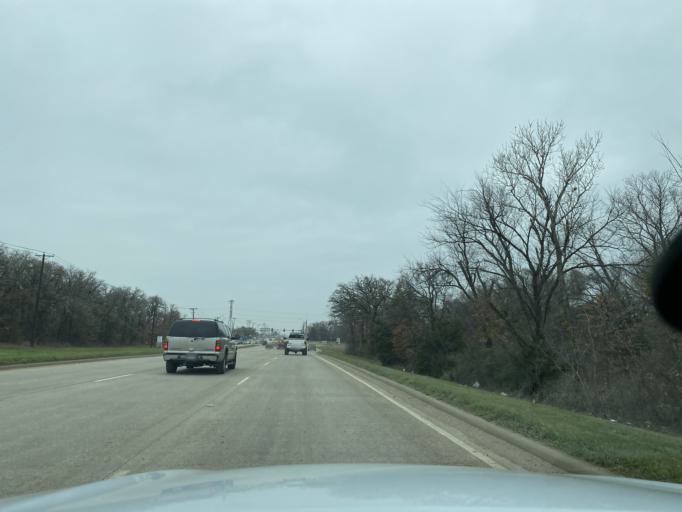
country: US
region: Texas
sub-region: Tarrant County
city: Euless
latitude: 32.8148
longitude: -97.0996
